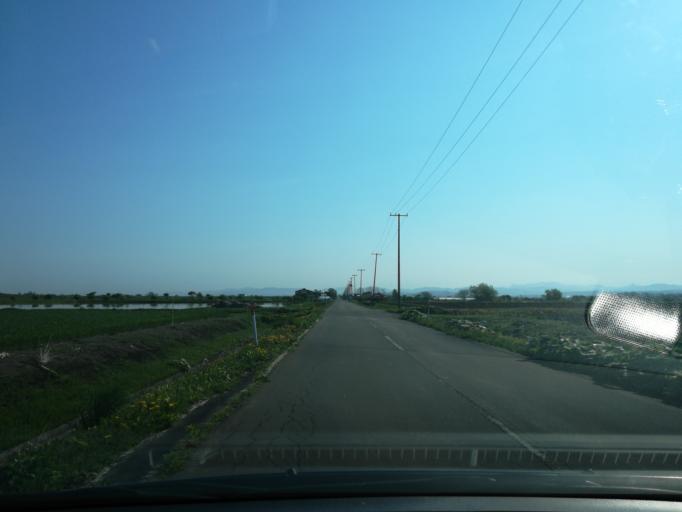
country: JP
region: Hokkaido
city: Ebetsu
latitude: 43.1248
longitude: 141.6641
